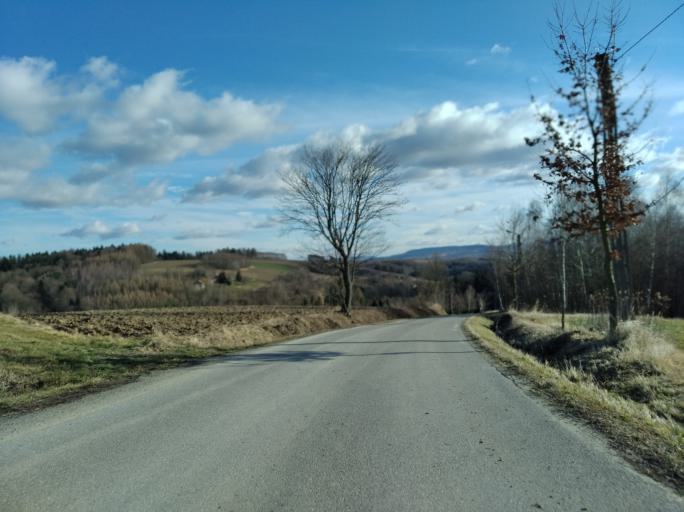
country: PL
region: Subcarpathian Voivodeship
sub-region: Powiat strzyzowski
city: Wisniowa
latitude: 49.8960
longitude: 21.7073
